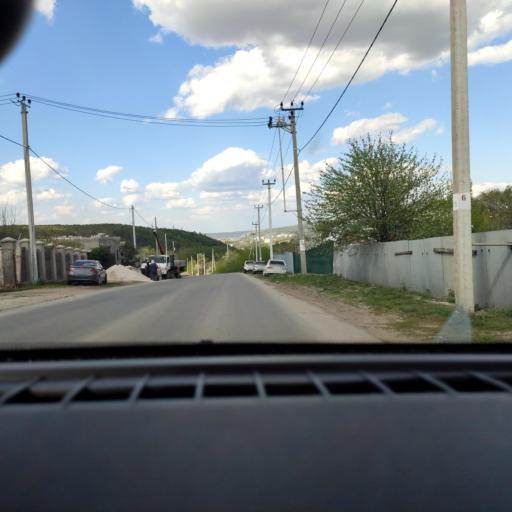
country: RU
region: Samara
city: Zhigulevsk
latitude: 53.3746
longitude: 49.4933
